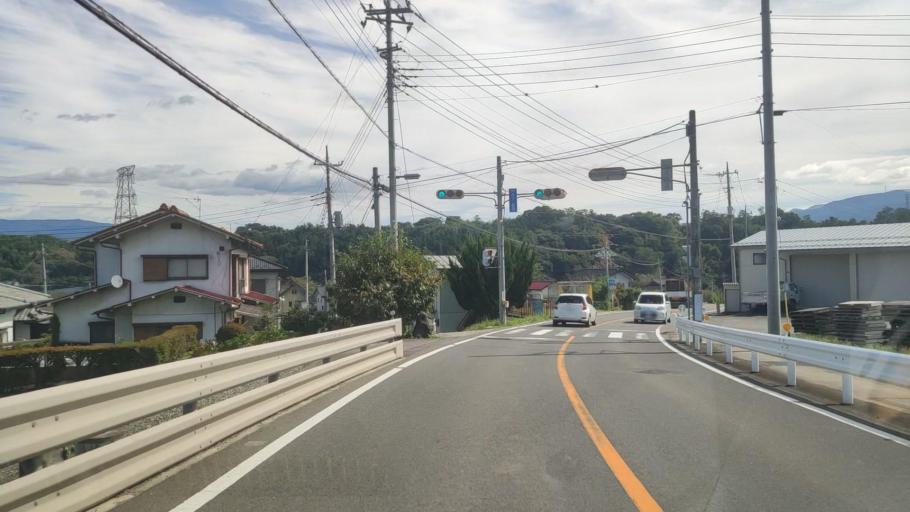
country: JP
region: Gunma
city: Numata
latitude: 36.6306
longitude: 139.0345
